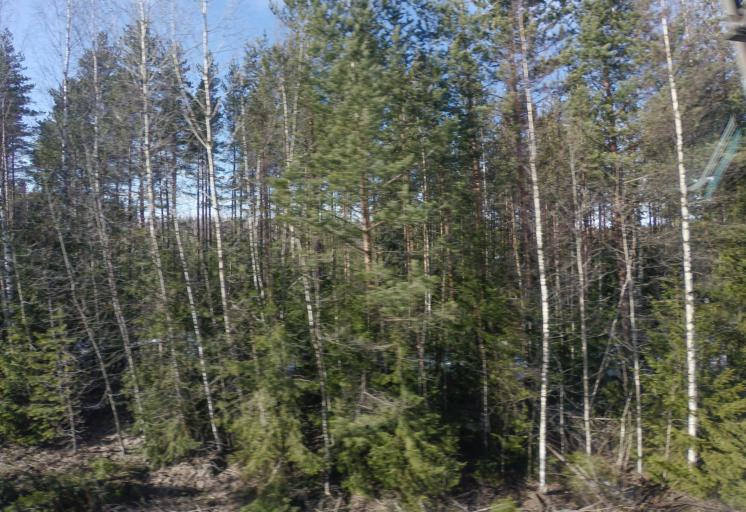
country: FI
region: South Karelia
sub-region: Lappeenranta
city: Joutseno
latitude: 61.0916
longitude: 28.3511
